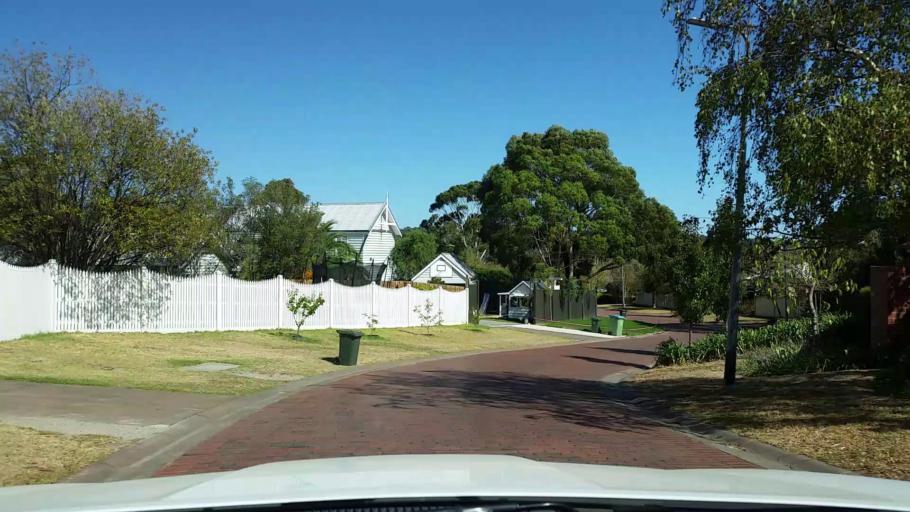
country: AU
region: Victoria
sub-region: Mornington Peninsula
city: Mount Martha
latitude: -38.2604
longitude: 145.0312
